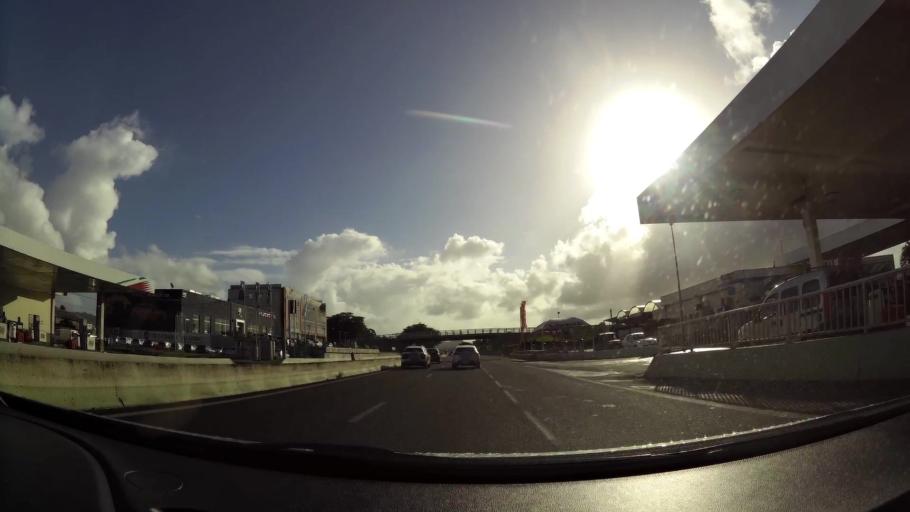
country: MQ
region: Martinique
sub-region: Martinique
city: Le Lamentin
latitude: 14.5966
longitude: -60.9952
